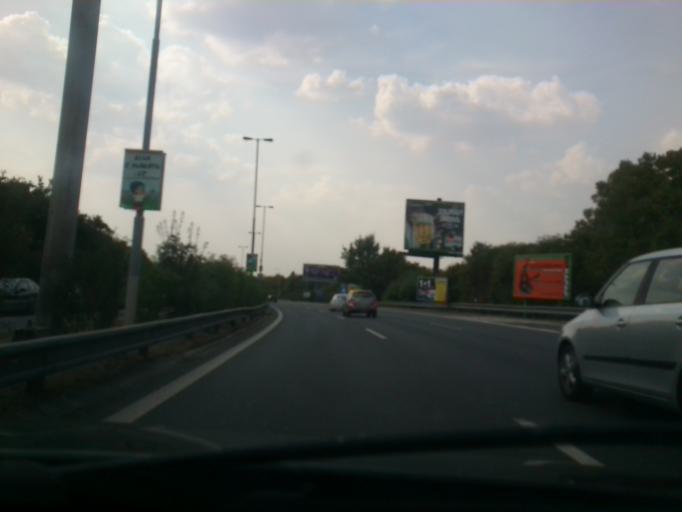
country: CZ
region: Central Bohemia
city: Vestec
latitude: 50.0390
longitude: 14.4878
